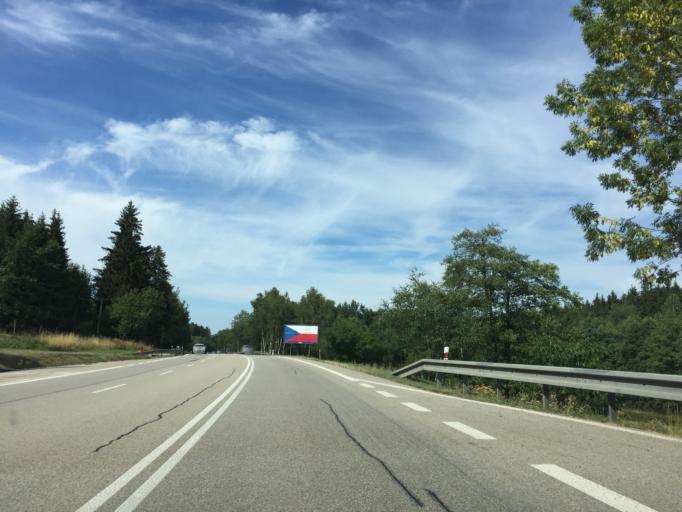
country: CZ
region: Central Bohemia
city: Votice
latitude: 49.6132
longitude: 14.6609
